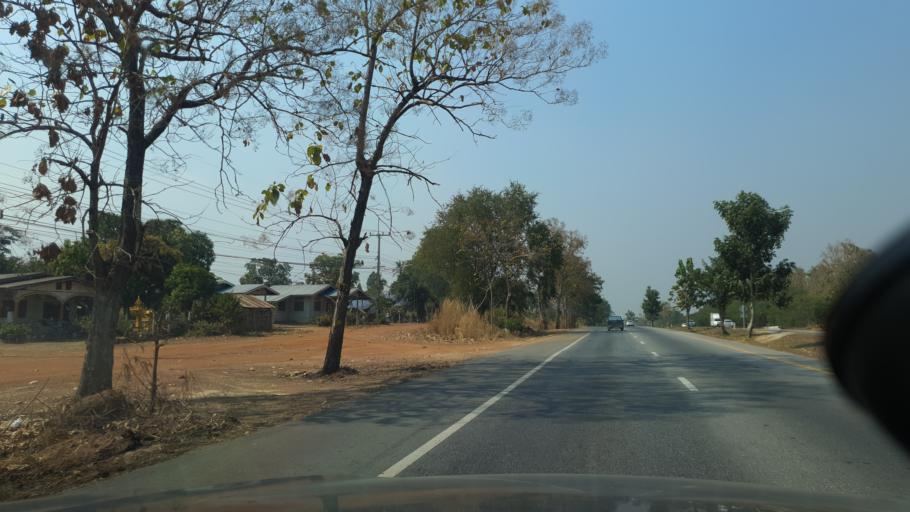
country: TH
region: Kamphaeng Phet
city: Kosamphi Nakhon
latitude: 16.5940
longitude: 99.4174
